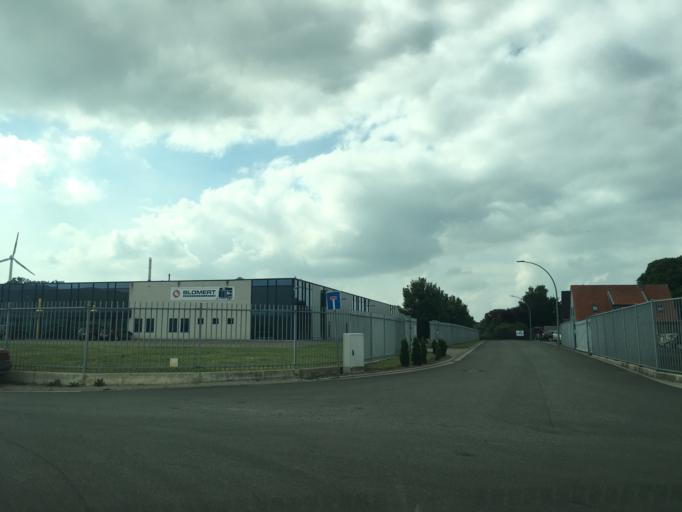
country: DE
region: North Rhine-Westphalia
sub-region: Regierungsbezirk Munster
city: Altenberge
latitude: 52.0763
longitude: 7.4553
